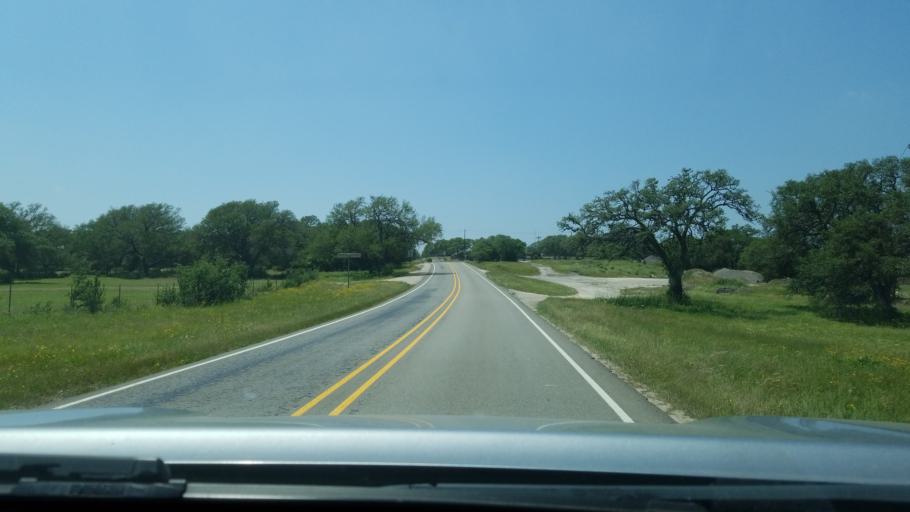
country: US
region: Texas
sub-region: Blanco County
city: Blanco
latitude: 30.0703
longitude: -98.4077
